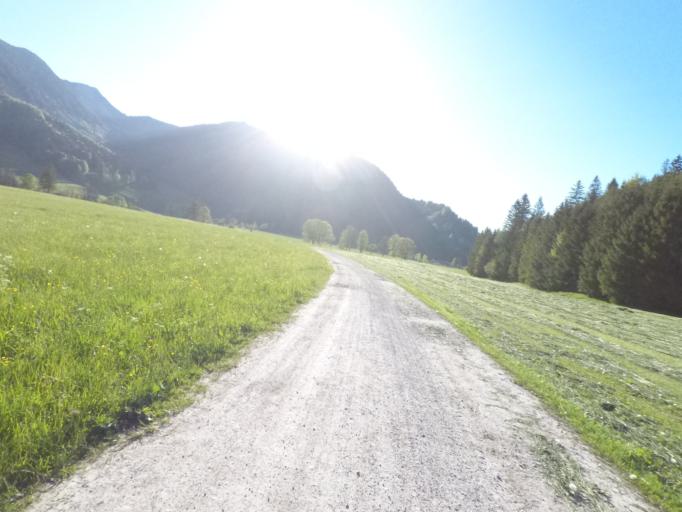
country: DE
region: Bavaria
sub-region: Upper Bavaria
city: Fischbachau
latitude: 47.6842
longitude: 11.9664
